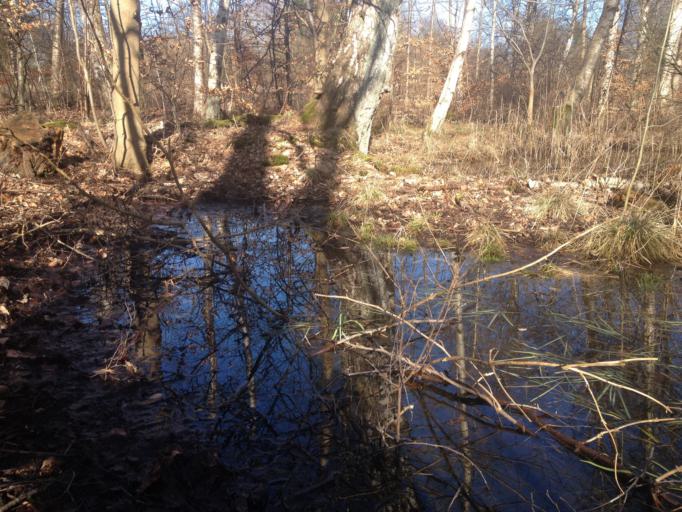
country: DK
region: Capital Region
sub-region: Egedal Kommune
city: Ganlose
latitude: 55.8179
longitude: 12.2581
